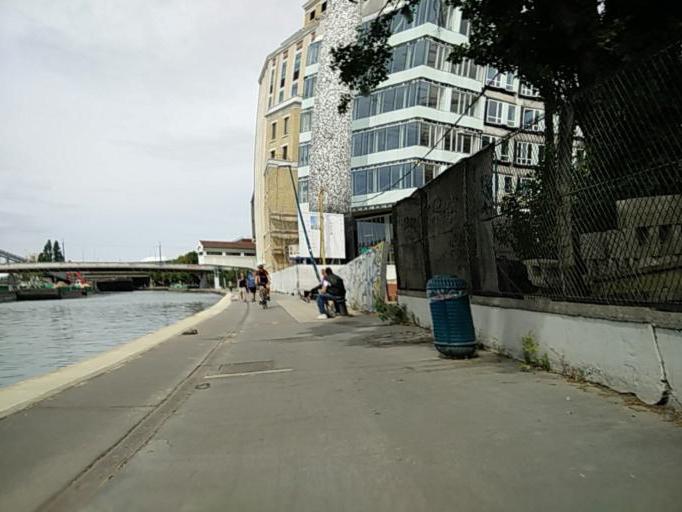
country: FR
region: Ile-de-France
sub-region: Departement de Seine-Saint-Denis
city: Pantin
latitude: 48.8963
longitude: 2.3991
